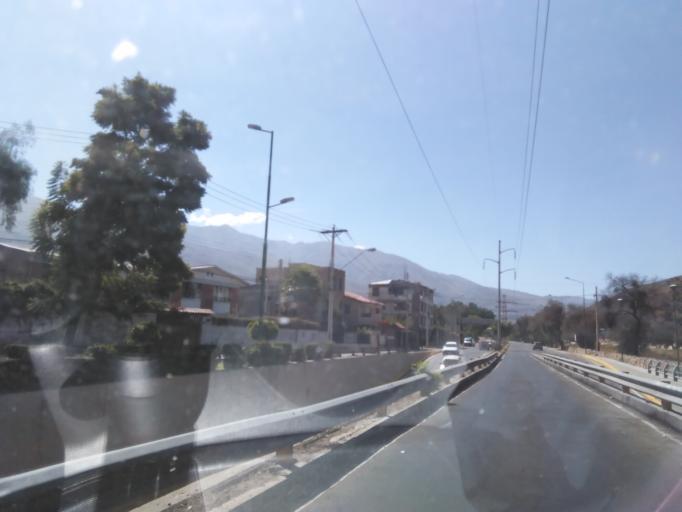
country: BO
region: Cochabamba
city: Cochabamba
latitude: -17.3768
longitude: -66.1424
